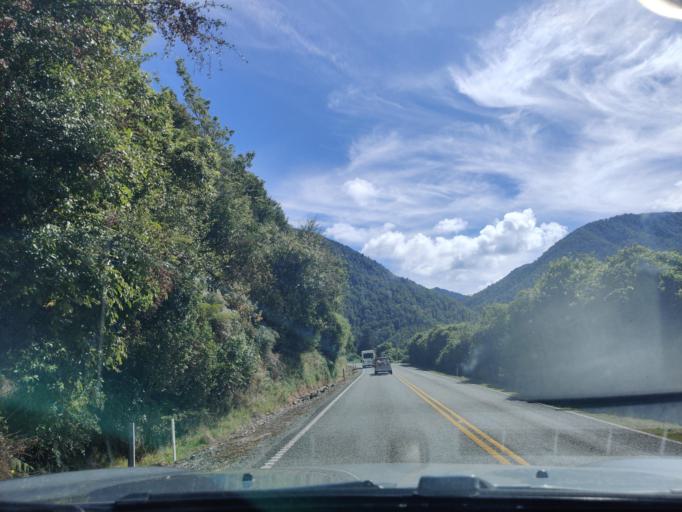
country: NZ
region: West Coast
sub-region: Buller District
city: Westport
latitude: -41.7736
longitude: 172.2387
